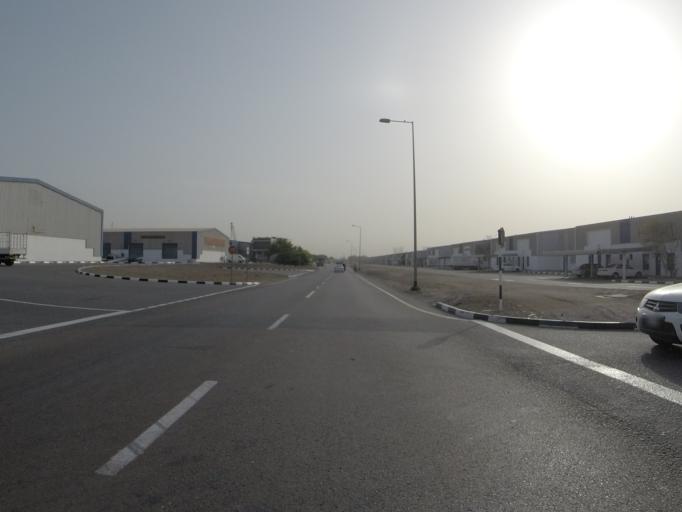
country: AE
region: Dubai
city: Dubai
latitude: 24.9635
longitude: 55.0638
